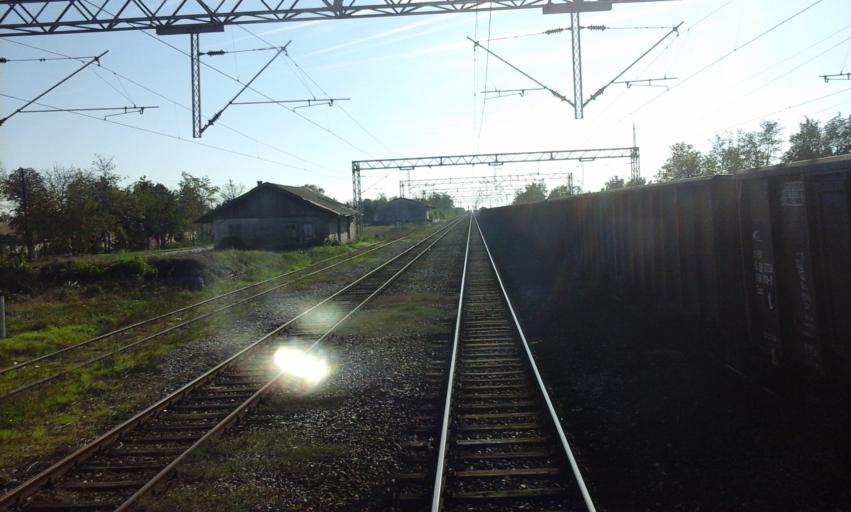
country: RS
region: Autonomna Pokrajina Vojvodina
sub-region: Severnobacki Okrug
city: Backa Topola
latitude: 45.9393
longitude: 19.6682
